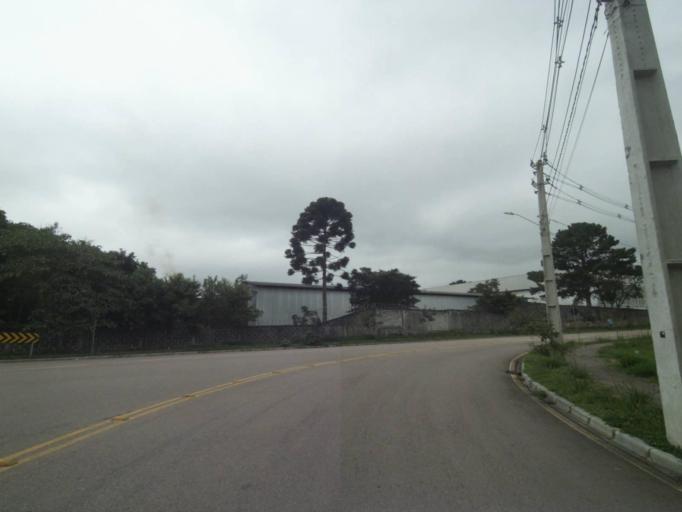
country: BR
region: Parana
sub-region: Sao Jose Dos Pinhais
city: Sao Jose dos Pinhais
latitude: -25.5524
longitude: -49.3074
